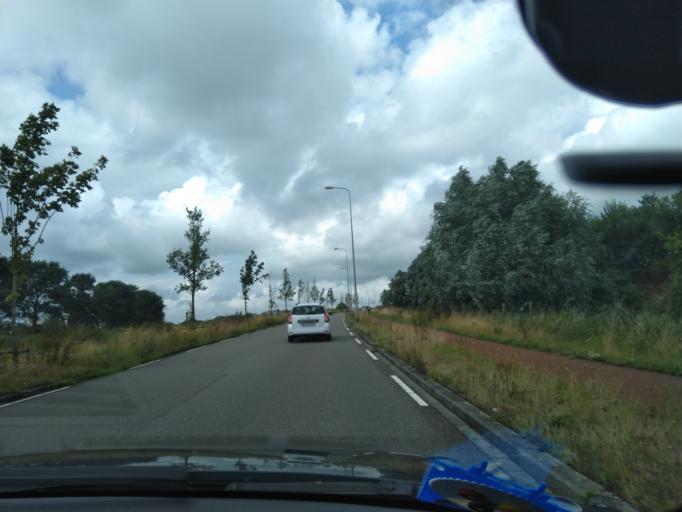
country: NL
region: Groningen
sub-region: Gemeente Groningen
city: Groningen
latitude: 53.2068
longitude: 6.5162
